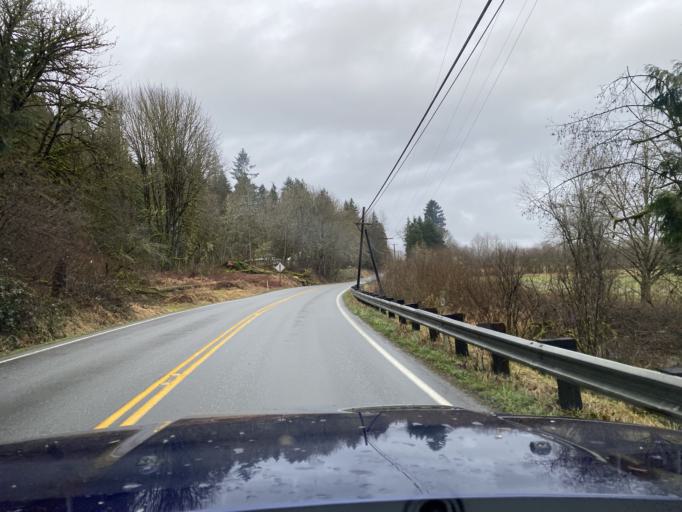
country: US
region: Washington
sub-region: King County
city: Duvall
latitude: 47.7404
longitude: -122.0125
